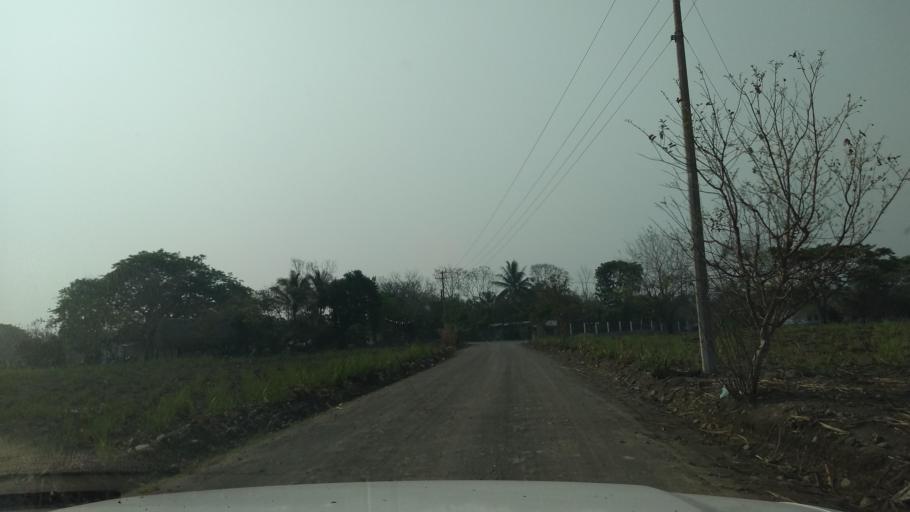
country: MX
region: Oaxaca
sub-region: Cosolapa
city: Cosolapa
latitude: 18.6247
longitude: -96.6081
